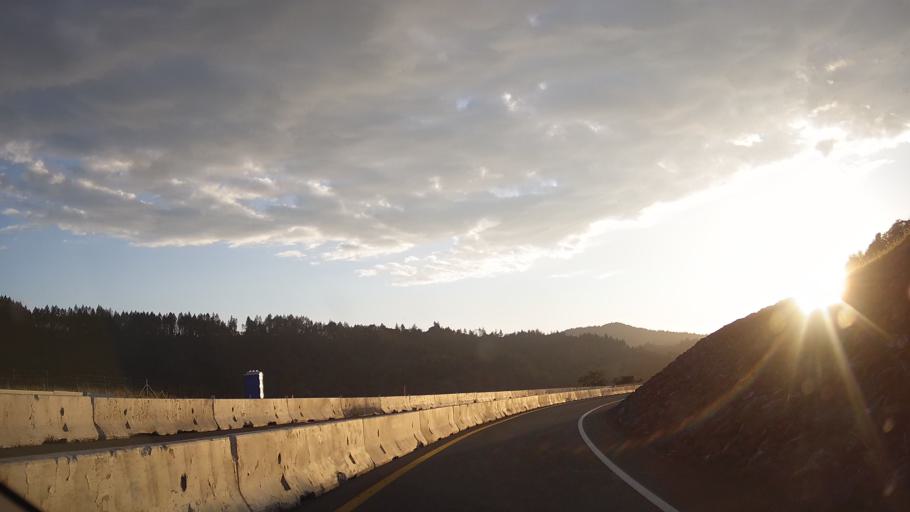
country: US
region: California
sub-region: Mendocino County
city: Redwood Valley
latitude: 39.3012
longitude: -123.2895
